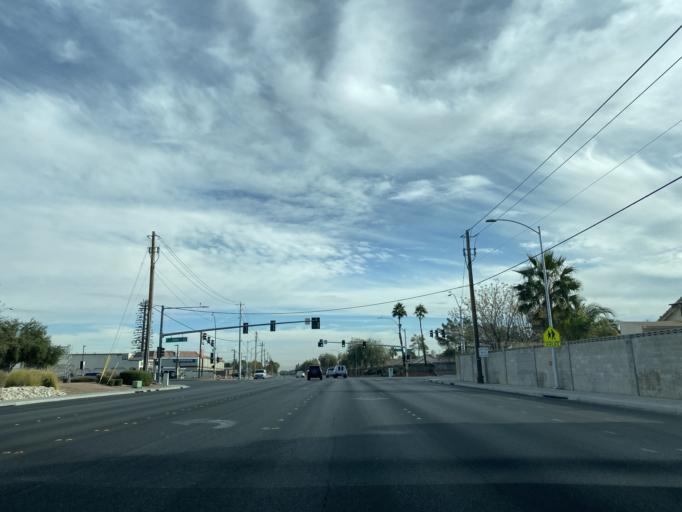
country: US
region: Nevada
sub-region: Clark County
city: Las Vegas
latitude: 36.2464
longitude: -115.2266
